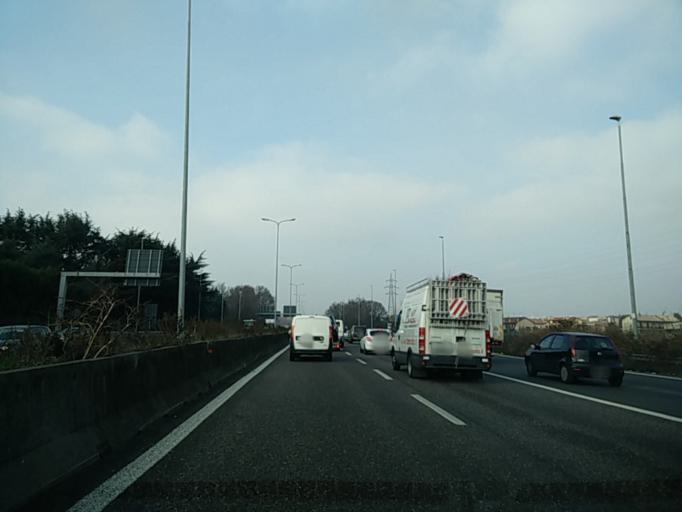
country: IT
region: Lombardy
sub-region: Citta metropolitana di Milano
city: Paderno Dugnano
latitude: 45.5646
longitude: 9.1776
